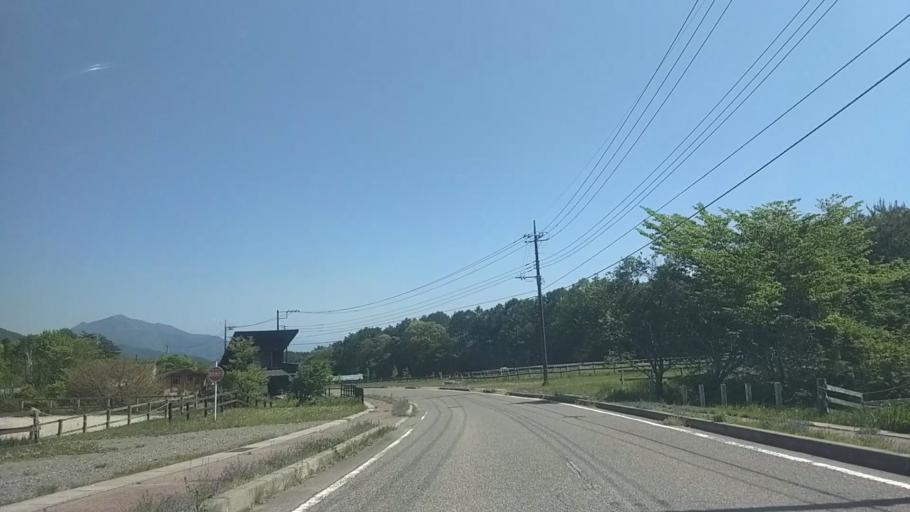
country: JP
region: Yamanashi
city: Nirasaki
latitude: 35.9083
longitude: 138.4321
